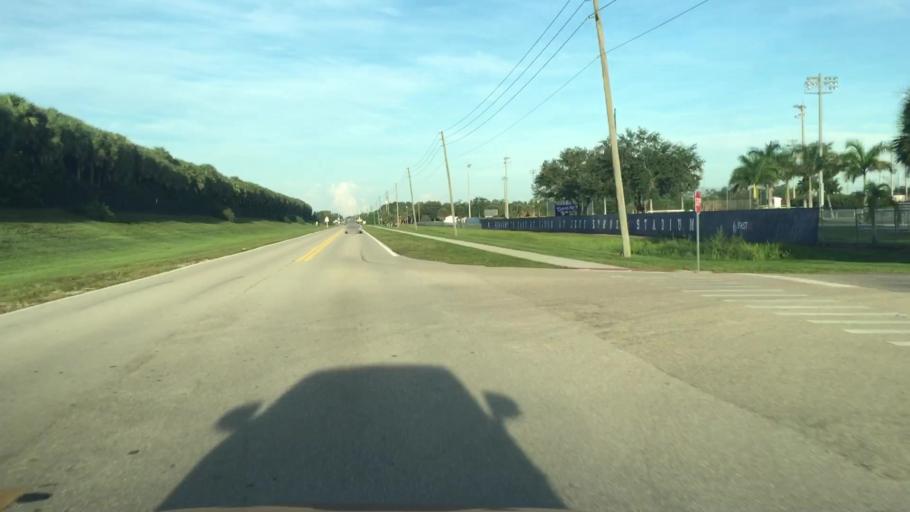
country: US
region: Florida
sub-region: Lee County
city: Estero
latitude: 26.4206
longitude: -81.7981
